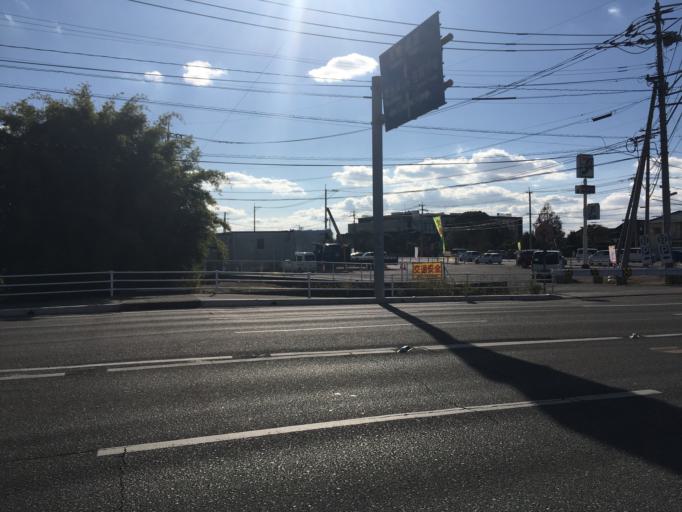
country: JP
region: Saga Prefecture
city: Saga-shi
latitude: 33.2394
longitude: 130.2951
